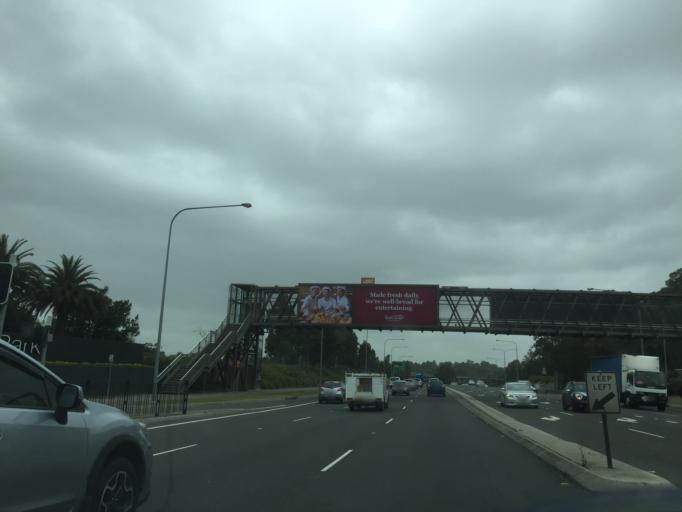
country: AU
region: New South Wales
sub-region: Blacktown
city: Blacktown
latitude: -33.7474
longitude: 150.9501
